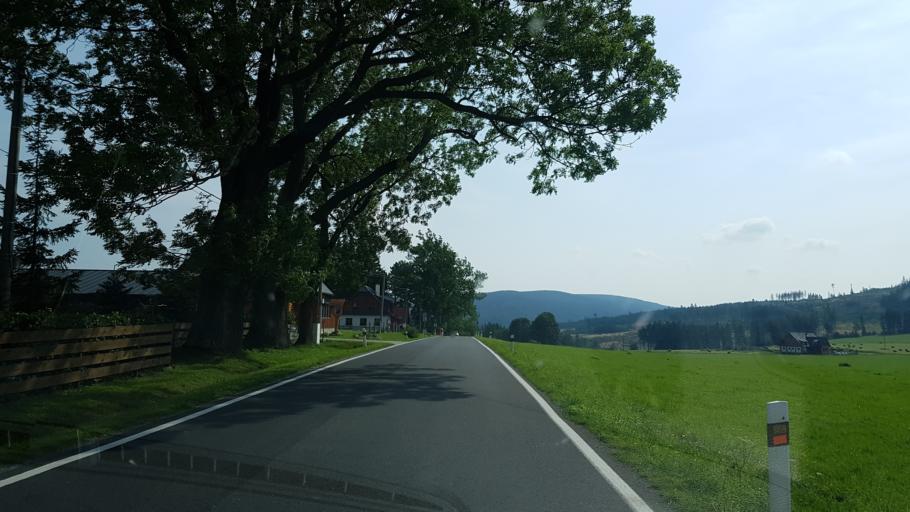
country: CZ
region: Olomoucky
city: Mikulovice
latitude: 50.2297
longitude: 17.3139
